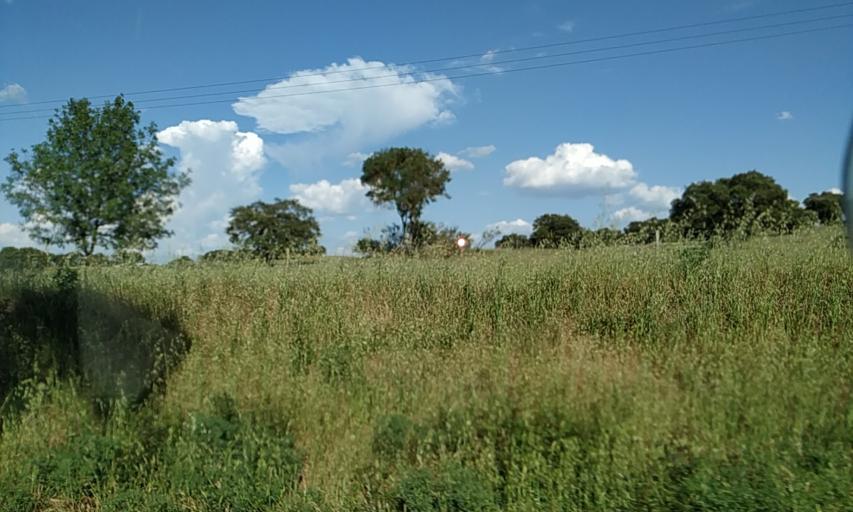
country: PT
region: Portalegre
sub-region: Fronteira
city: Fronteira
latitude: 39.0178
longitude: -7.4651
